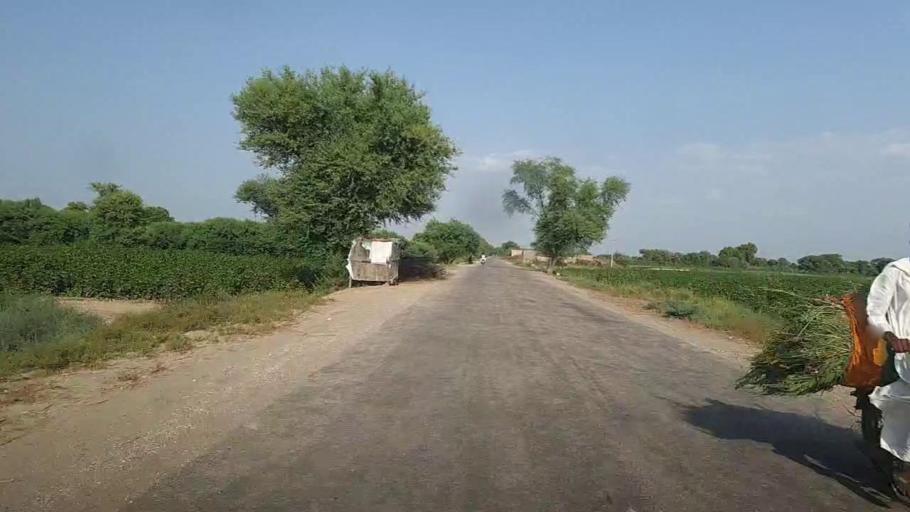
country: PK
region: Sindh
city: Khairpur
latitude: 28.0760
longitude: 69.8048
